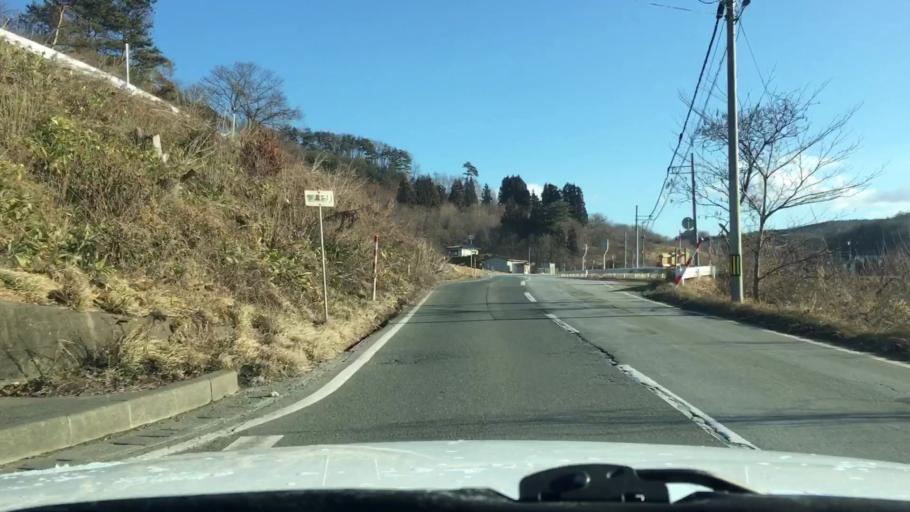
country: JP
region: Iwate
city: Morioka-shi
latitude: 39.6622
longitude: 141.1986
